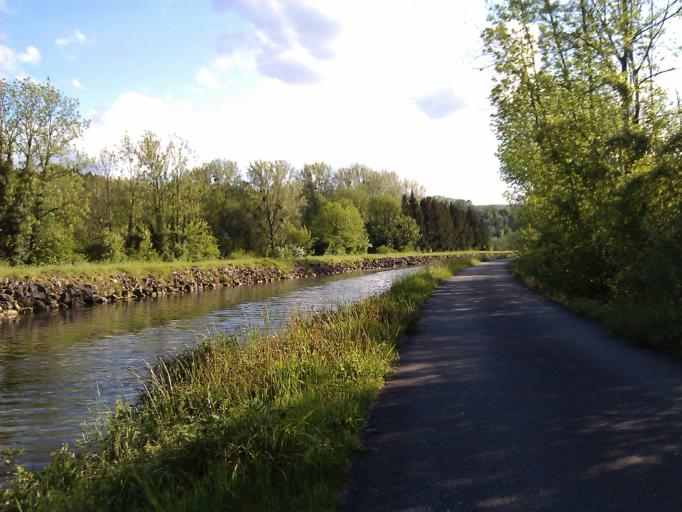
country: FR
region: Franche-Comte
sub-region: Departement du Doubs
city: Clerval
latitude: 47.4176
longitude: 6.5543
